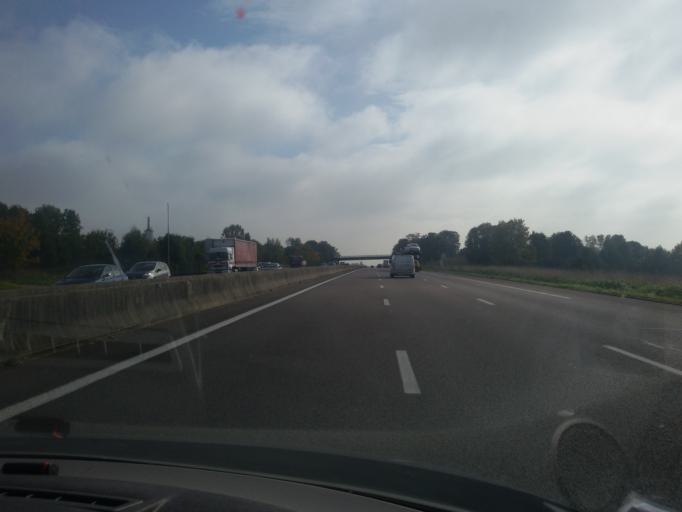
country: FR
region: Haute-Normandie
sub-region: Departement de l'Eure
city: Saint-Pierre-du-Vauvray
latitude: 49.2229
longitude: 1.2112
